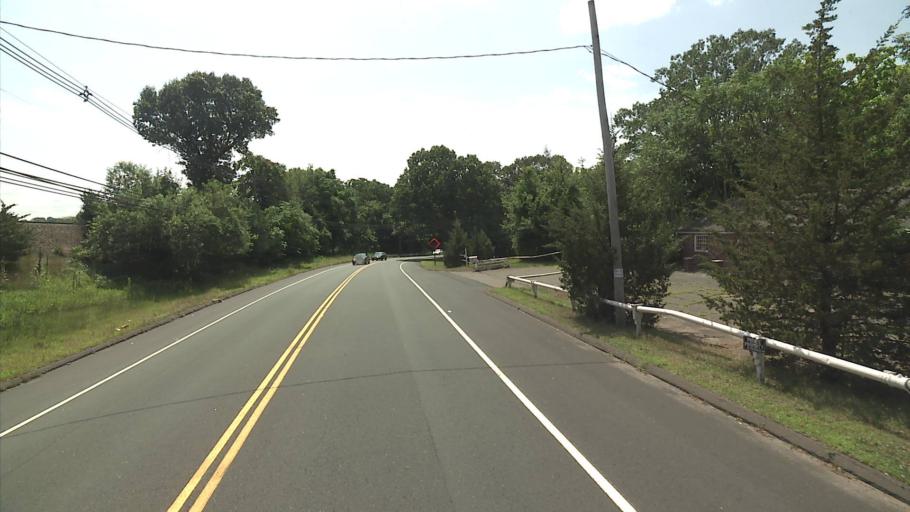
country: US
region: Connecticut
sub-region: New Haven County
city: Meriden
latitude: 41.4994
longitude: -72.8156
